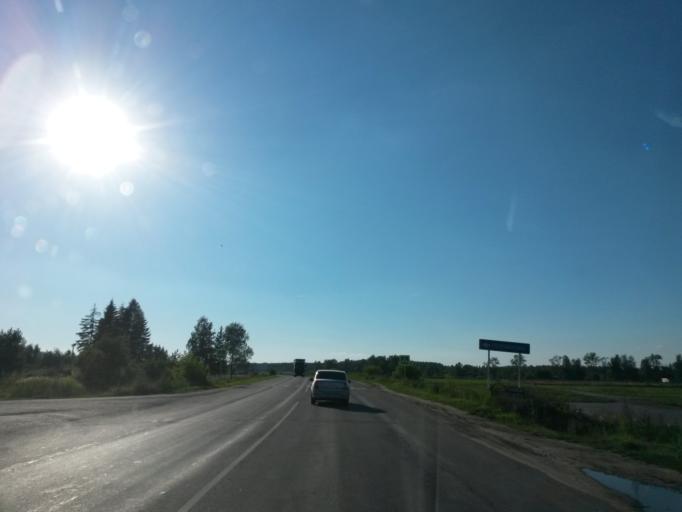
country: RU
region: Ivanovo
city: Novo-Talitsy
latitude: 57.0118
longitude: 40.8313
